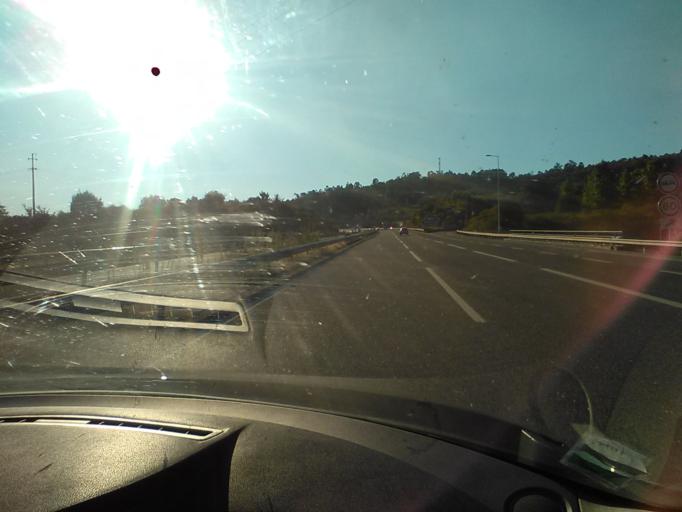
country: PT
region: Braga
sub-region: Vizela
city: Vizela
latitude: 41.4020
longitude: -8.2523
